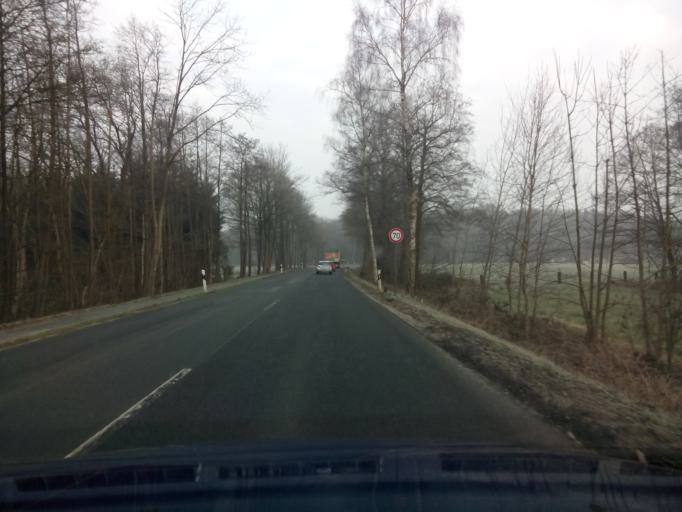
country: DE
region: Lower Saxony
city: Schiffdorf
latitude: 53.5994
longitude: 8.6675
